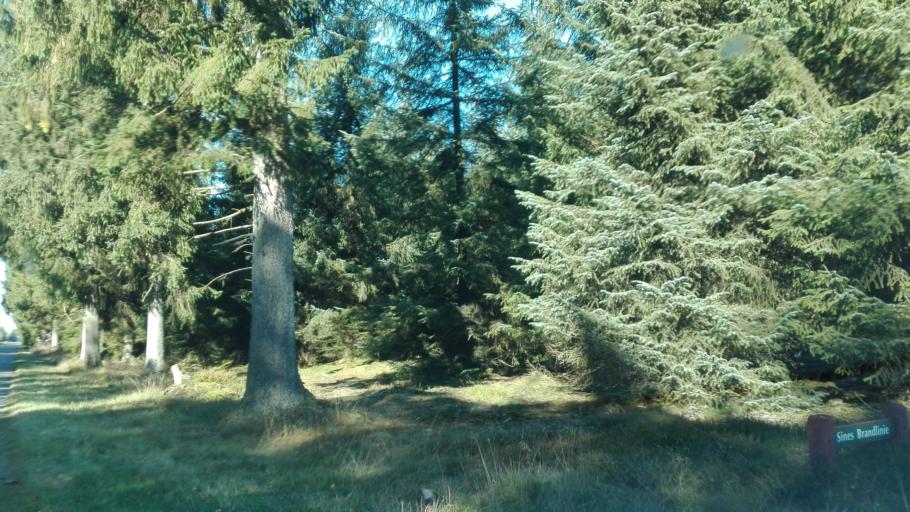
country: DK
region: Central Jutland
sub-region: Ikast-Brande Kommune
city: Bording Kirkeby
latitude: 56.0731
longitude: 9.3676
